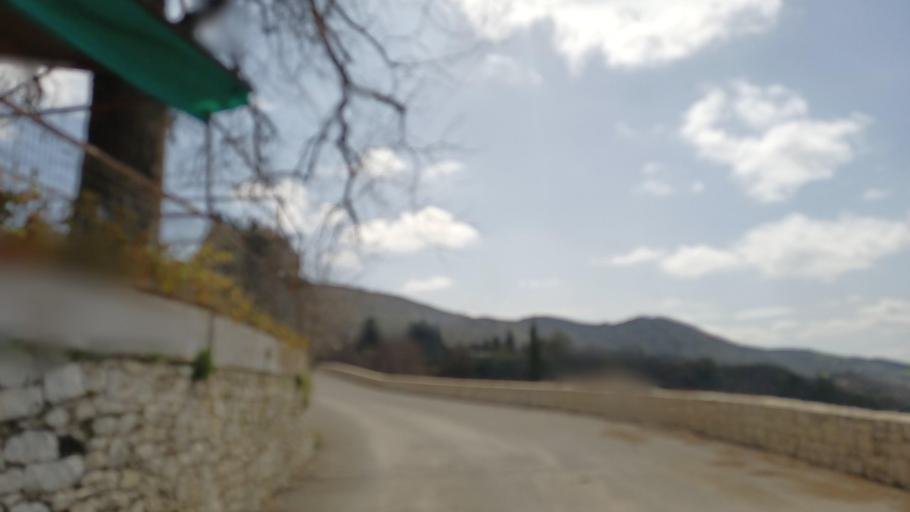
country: CY
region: Limassol
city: Pachna
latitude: 34.8600
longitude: 32.7524
